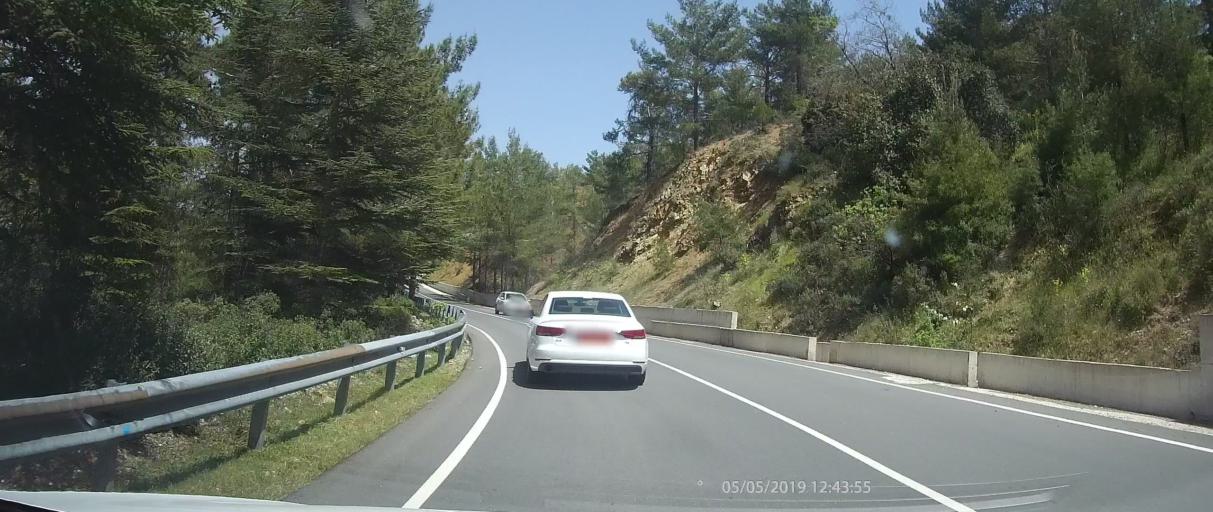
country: CY
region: Lefkosia
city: Kakopetria
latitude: 34.9676
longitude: 32.8170
